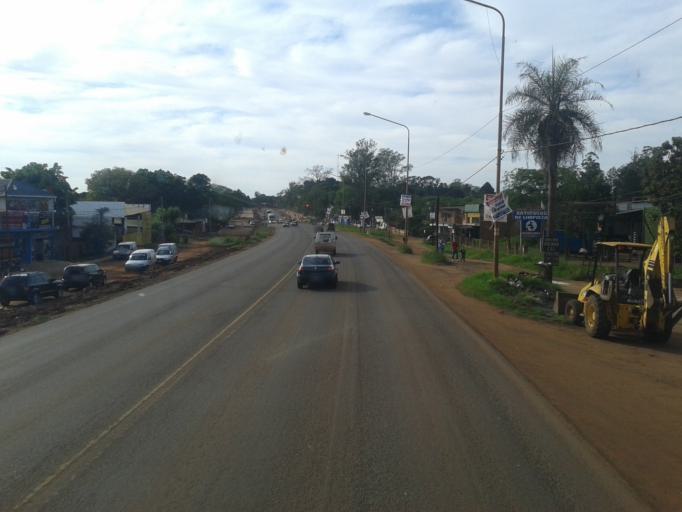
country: AR
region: Misiones
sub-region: Departamento de Capital
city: Posadas
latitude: -27.4248
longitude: -55.8972
